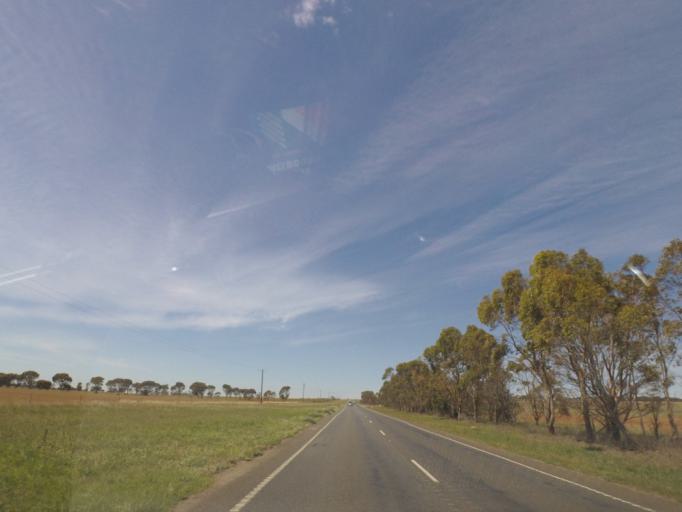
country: AU
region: Victoria
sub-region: Moorabool
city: Bacchus Marsh
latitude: -37.7650
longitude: 144.4402
